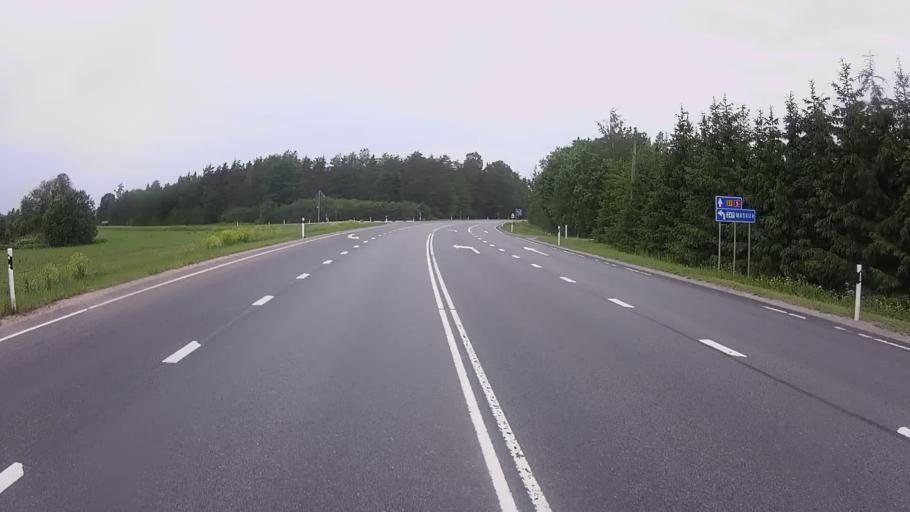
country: EE
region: Paernumaa
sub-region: Vaendra vald (alev)
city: Vandra
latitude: 58.6516
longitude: 25.0034
